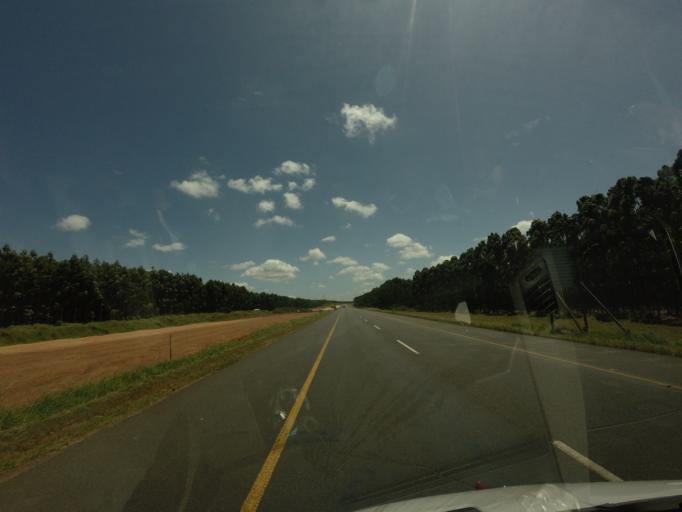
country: ZA
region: KwaZulu-Natal
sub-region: uThungulu District Municipality
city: Empangeni
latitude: -28.7464
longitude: 31.9373
